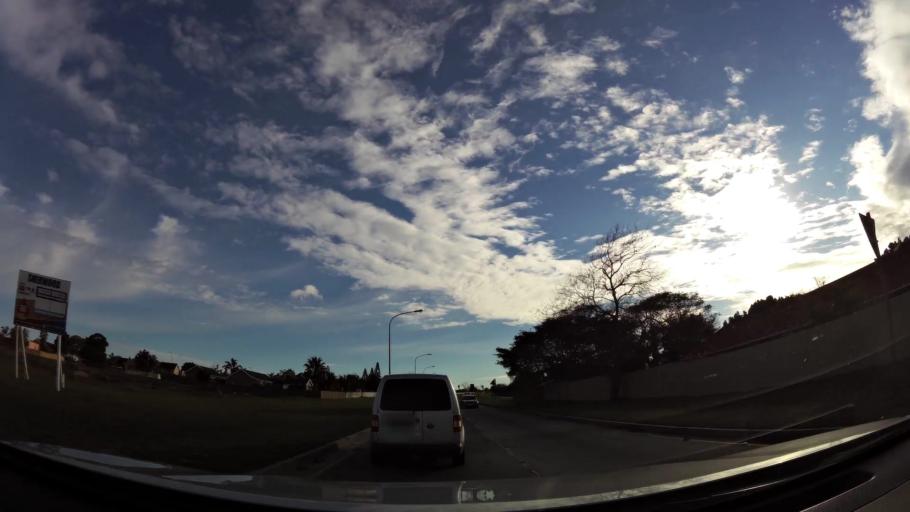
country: ZA
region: Eastern Cape
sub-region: Nelson Mandela Bay Metropolitan Municipality
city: Port Elizabeth
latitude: -33.9596
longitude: 25.4867
